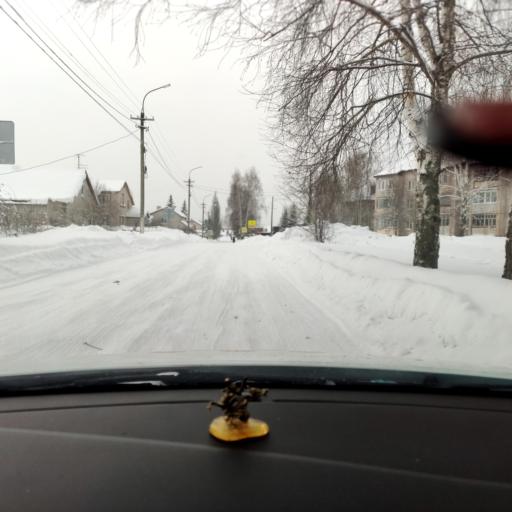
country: RU
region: Tatarstan
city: Stolbishchi
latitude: 55.6106
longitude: 49.1419
